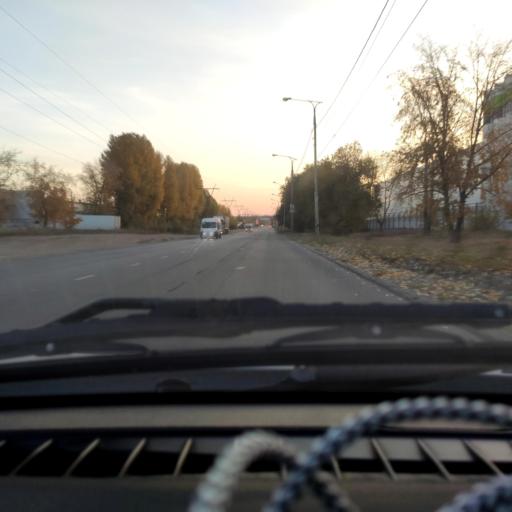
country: RU
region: Samara
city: Zhigulevsk
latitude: 53.4773
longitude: 49.4915
